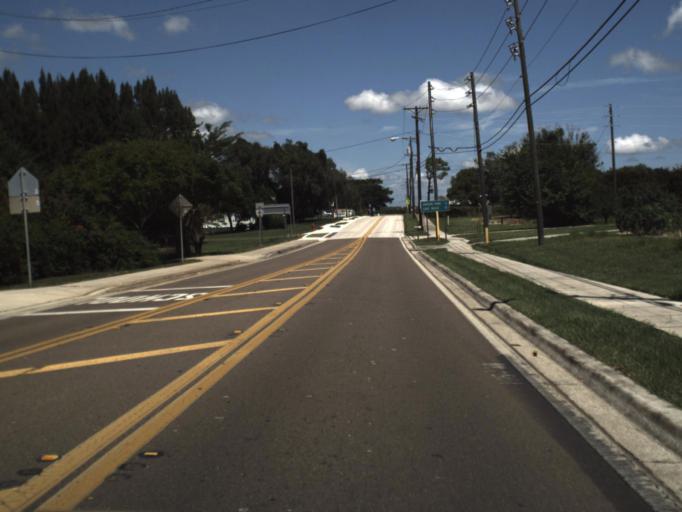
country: US
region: Florida
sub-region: Polk County
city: Frostproof
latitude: 27.7567
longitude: -81.5306
